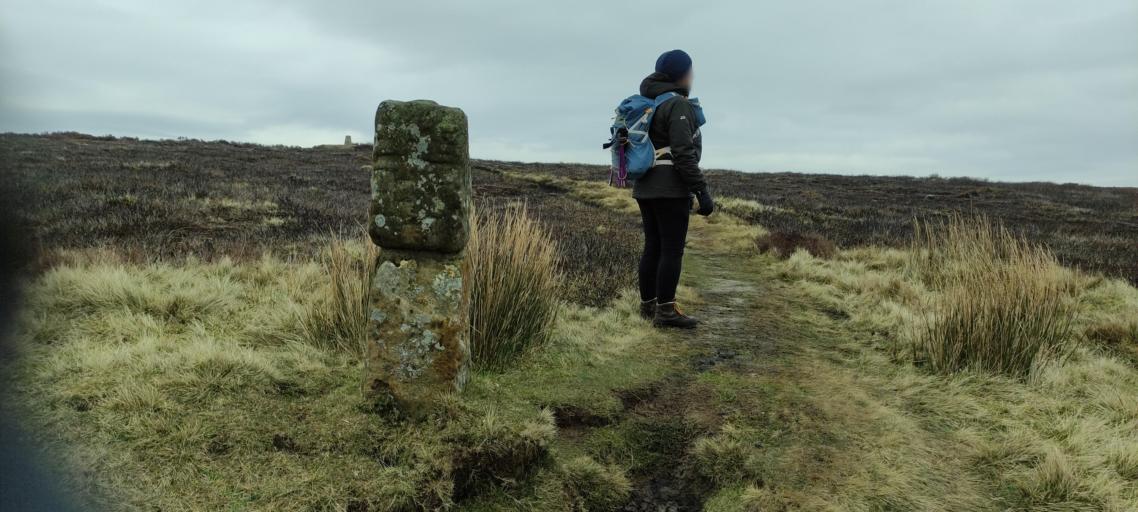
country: GB
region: England
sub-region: North Yorkshire
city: Bilsdale
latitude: 54.4056
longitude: -1.0860
